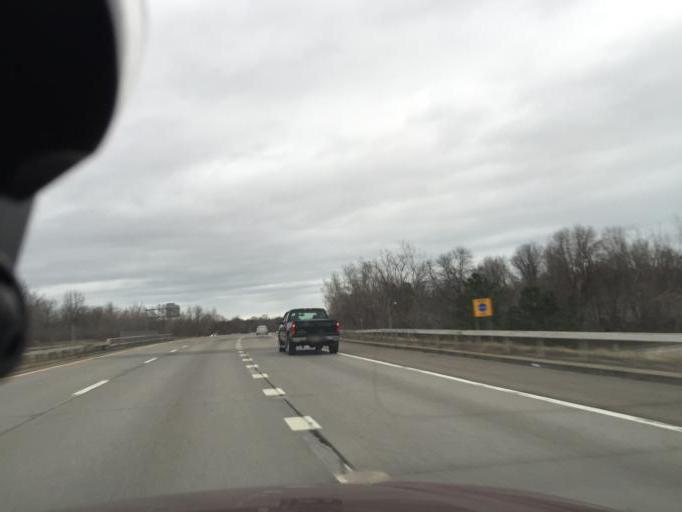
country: US
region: New York
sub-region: Monroe County
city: Greece
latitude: 43.2231
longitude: -77.6747
